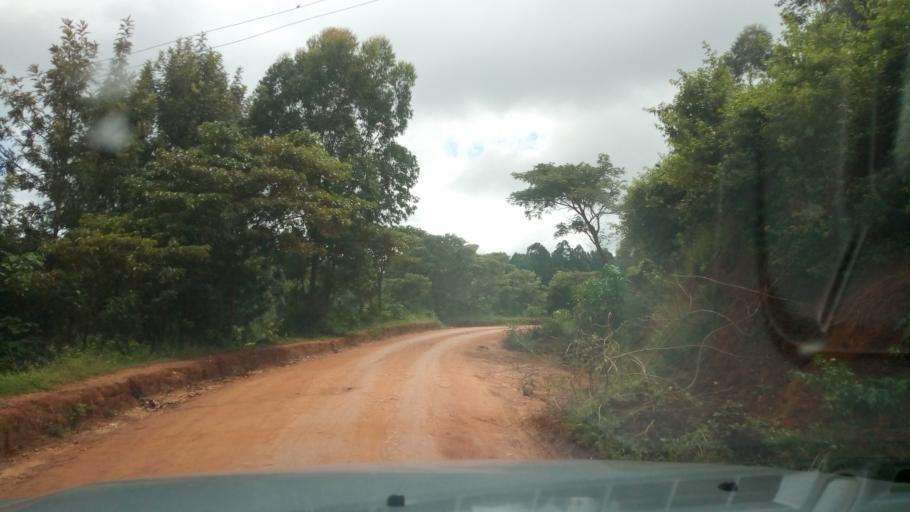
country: KE
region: Makueni
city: Wote
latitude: -1.6730
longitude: 37.4487
